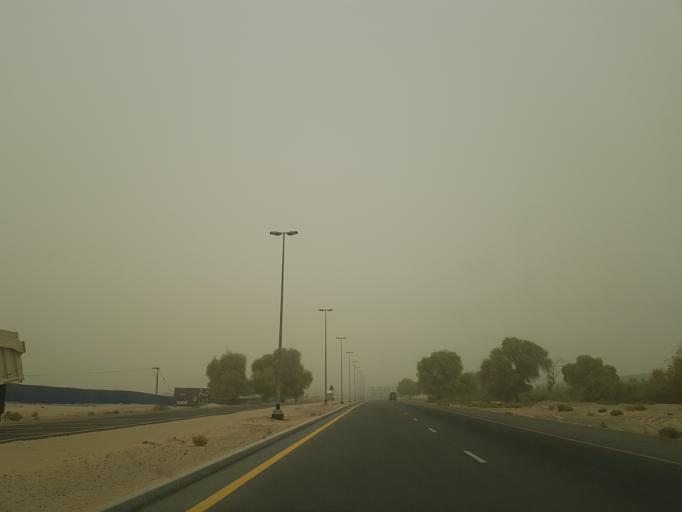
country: AE
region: Dubai
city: Dubai
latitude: 25.1424
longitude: 55.2886
